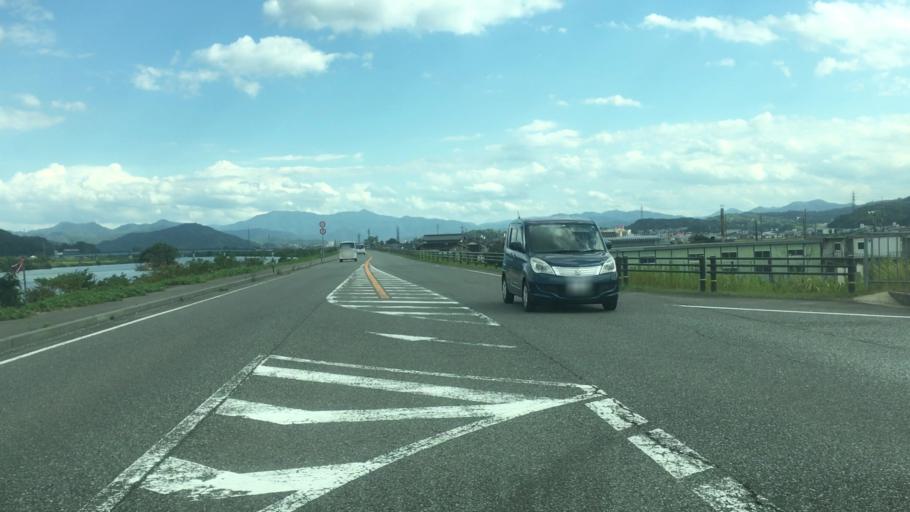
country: JP
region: Hyogo
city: Toyooka
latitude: 35.5684
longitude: 134.8097
